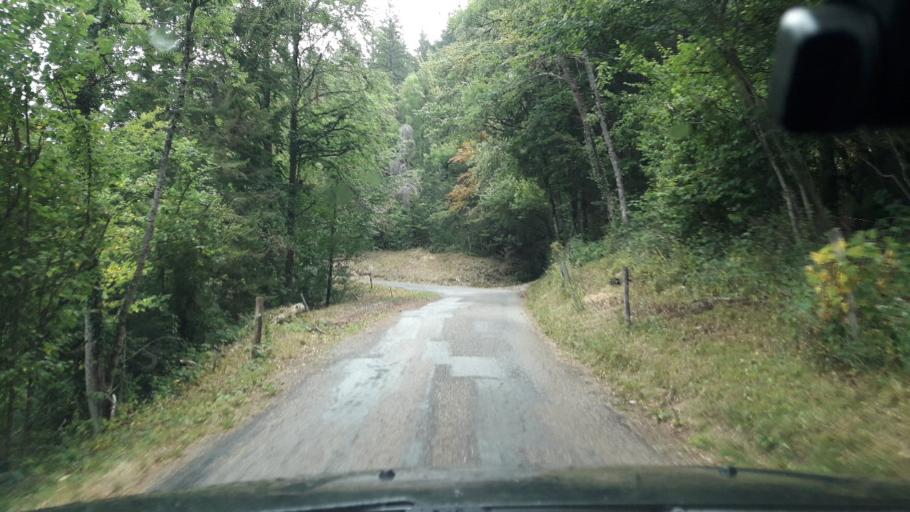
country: FR
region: Rhone-Alpes
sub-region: Departement de la Savoie
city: Vimines
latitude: 45.4636
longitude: 5.8902
